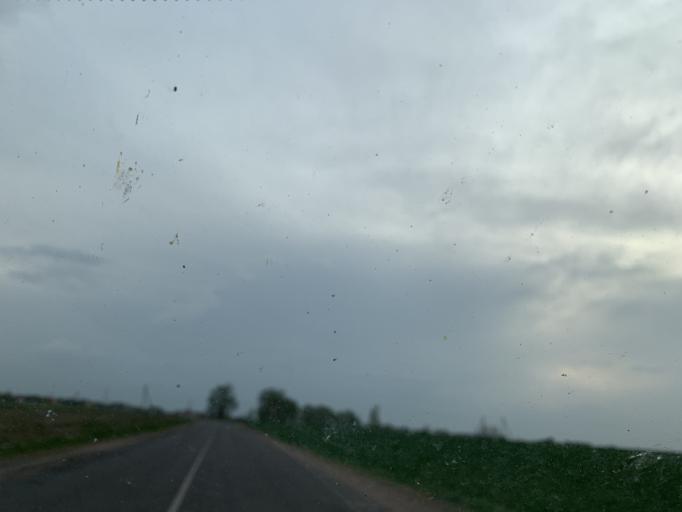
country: BY
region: Minsk
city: Kapyl'
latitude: 53.2693
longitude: 26.9597
